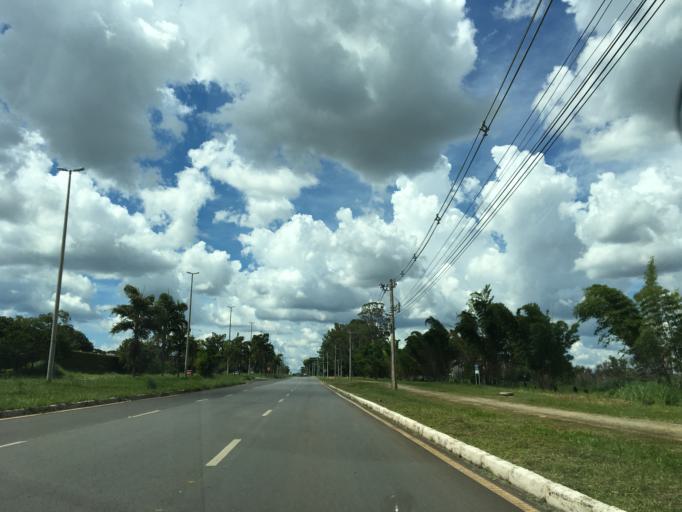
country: BR
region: Federal District
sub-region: Brasilia
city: Brasilia
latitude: -15.7784
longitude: -47.8714
